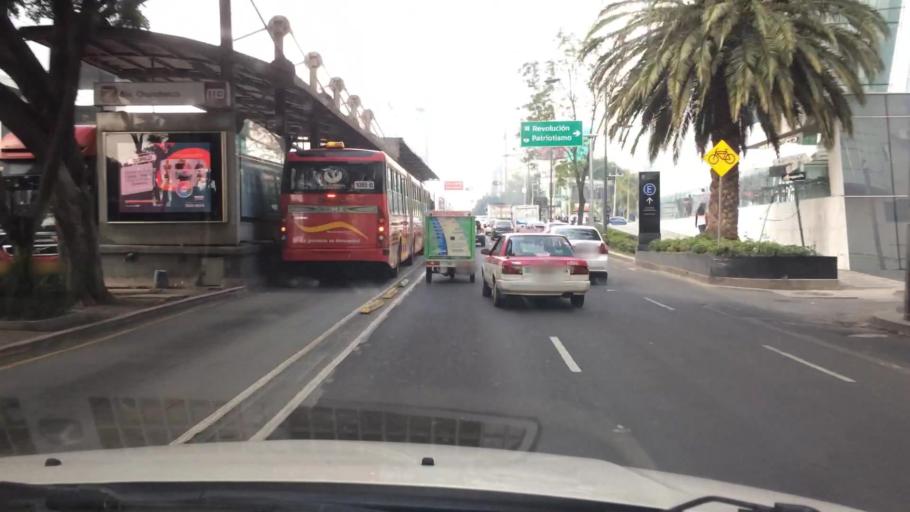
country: MX
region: Mexico City
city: Colonia del Valle
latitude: 19.3693
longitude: -99.1805
